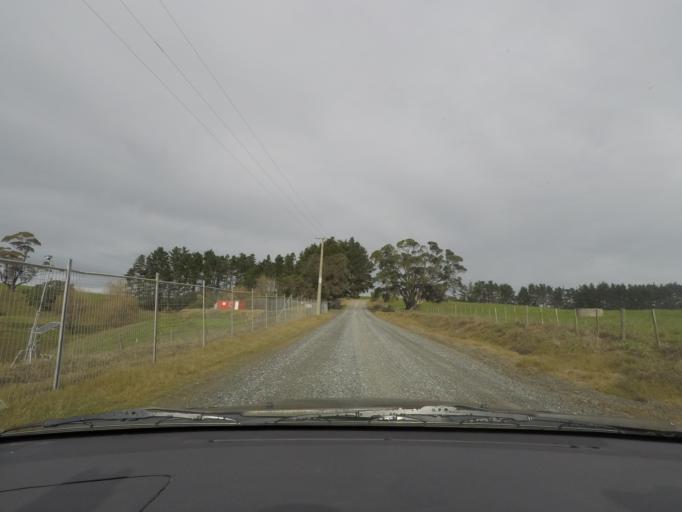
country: NZ
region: Auckland
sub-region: Auckland
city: Warkworth
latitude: -36.4519
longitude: 174.7505
